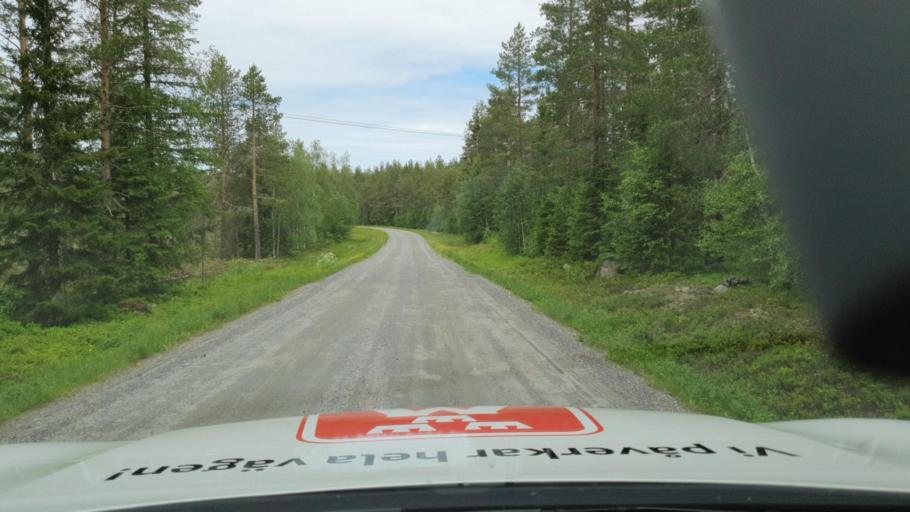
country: SE
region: Vaesterbotten
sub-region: Skelleftea Kommun
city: Langsele
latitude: 64.4832
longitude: 20.2577
